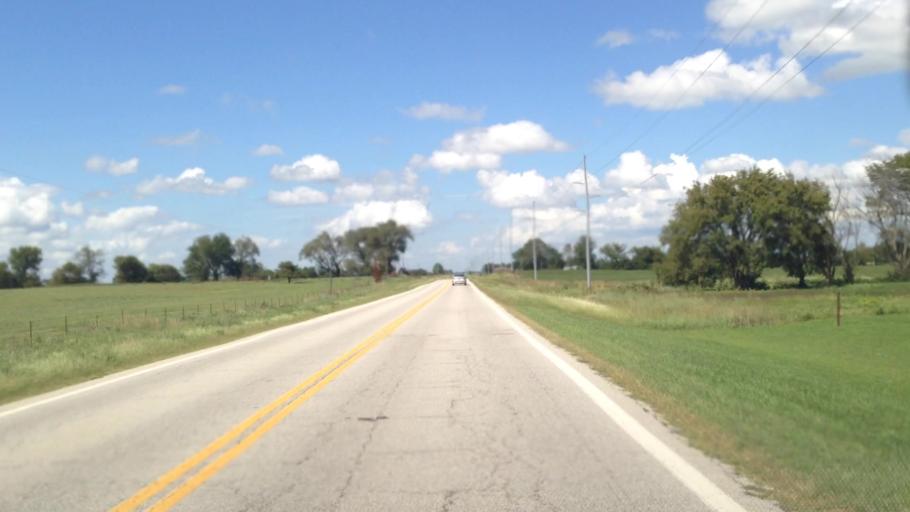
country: US
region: Kansas
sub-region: Labette County
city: Chetopa
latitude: 36.9467
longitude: -95.0829
